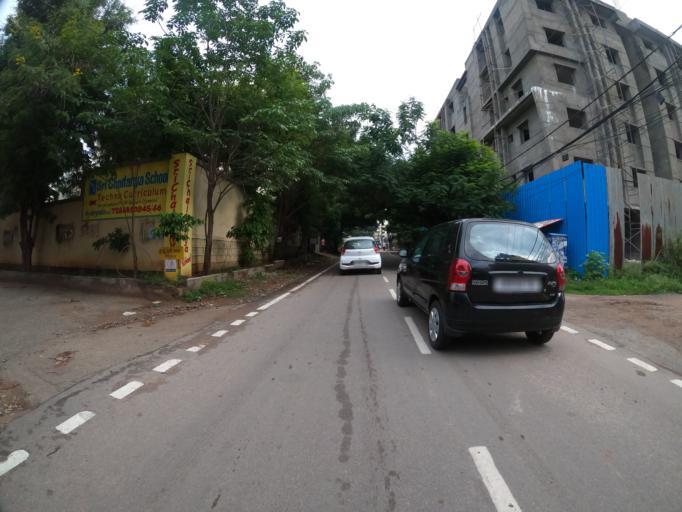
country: IN
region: Telangana
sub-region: Hyderabad
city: Hyderabad
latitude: 17.3700
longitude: 78.4228
